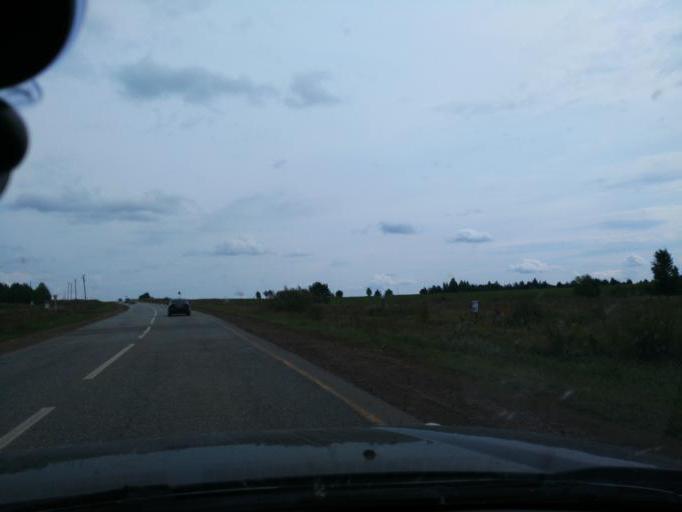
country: RU
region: Perm
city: Kuyeda
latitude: 56.4691
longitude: 55.7285
